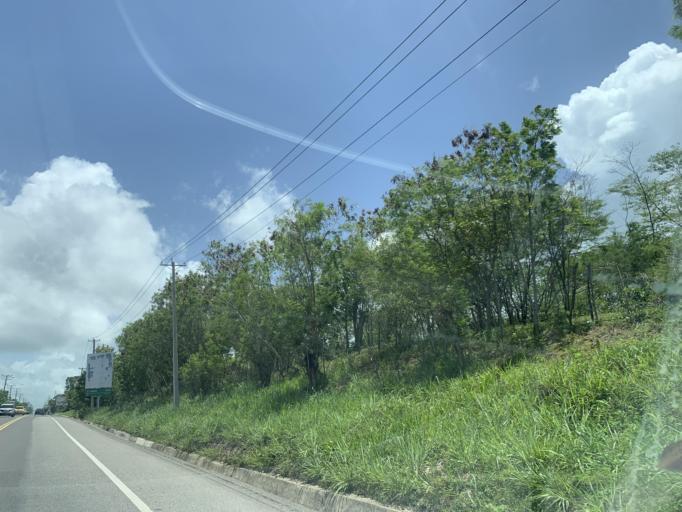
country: DO
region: Puerto Plata
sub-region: Puerto Plata
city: Puerto Plata
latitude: 19.7366
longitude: -70.6305
